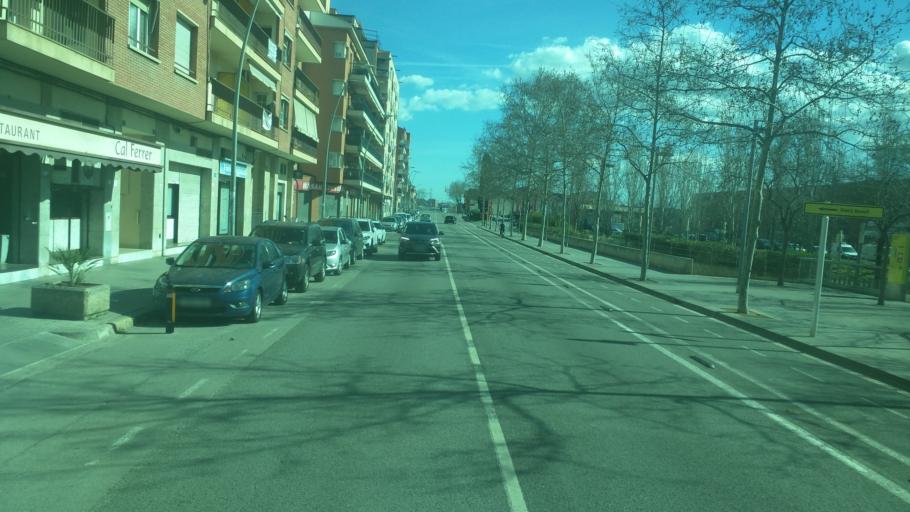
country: ES
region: Catalonia
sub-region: Provincia de Barcelona
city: Molins de Rei
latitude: 41.4057
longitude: 2.0244
